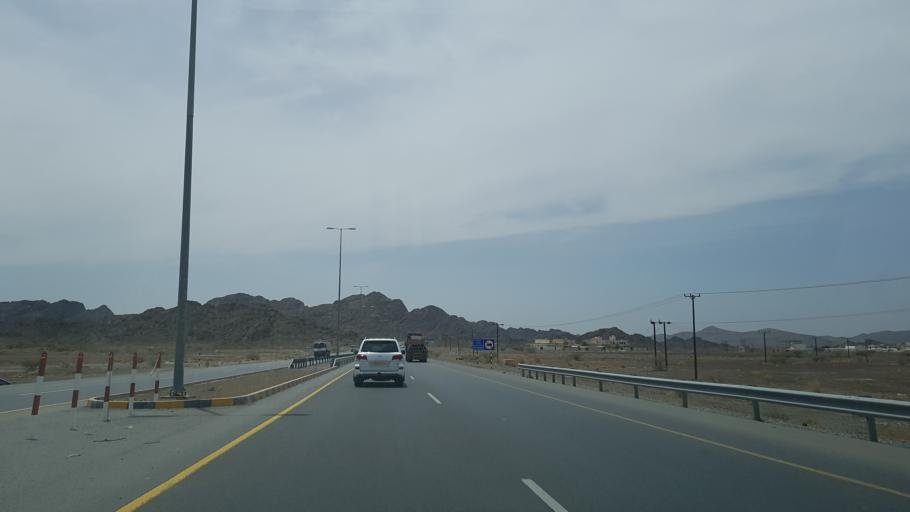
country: OM
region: Muhafazat ad Dakhiliyah
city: Izki
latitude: 22.9336
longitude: 57.7896
